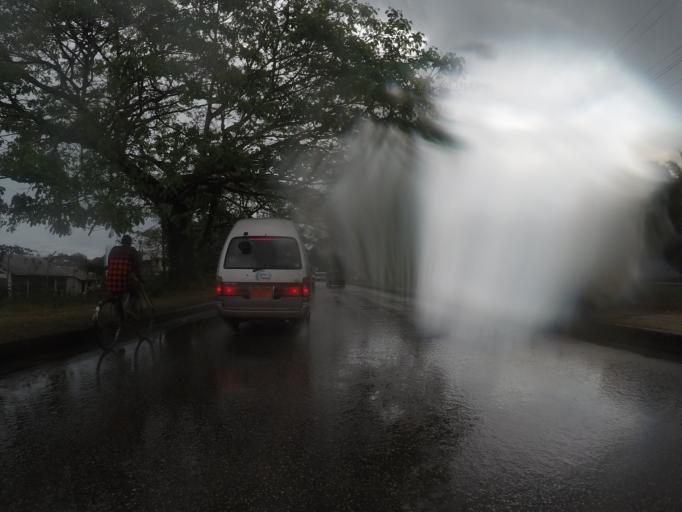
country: TZ
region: Zanzibar Urban/West
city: Zanzibar
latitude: -6.1347
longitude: 39.2156
